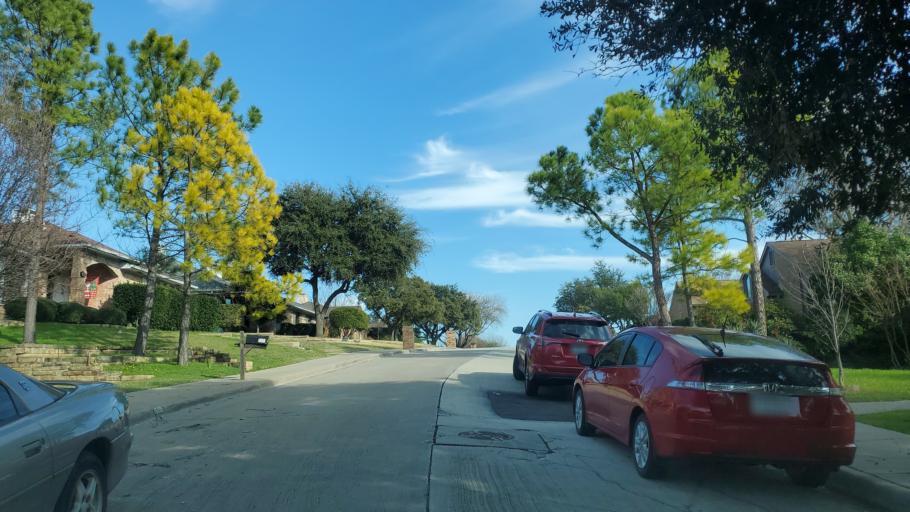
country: US
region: Texas
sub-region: Dallas County
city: Carrollton
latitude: 32.9878
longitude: -96.8978
